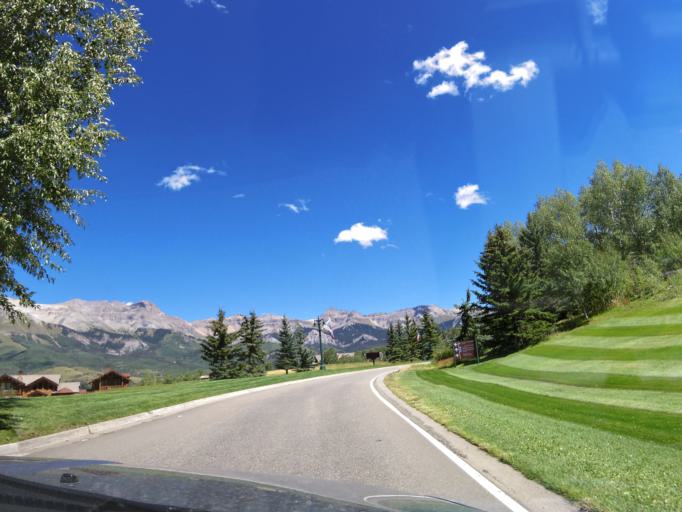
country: US
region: Colorado
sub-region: San Miguel County
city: Mountain Village
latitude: 37.9334
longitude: -107.8775
